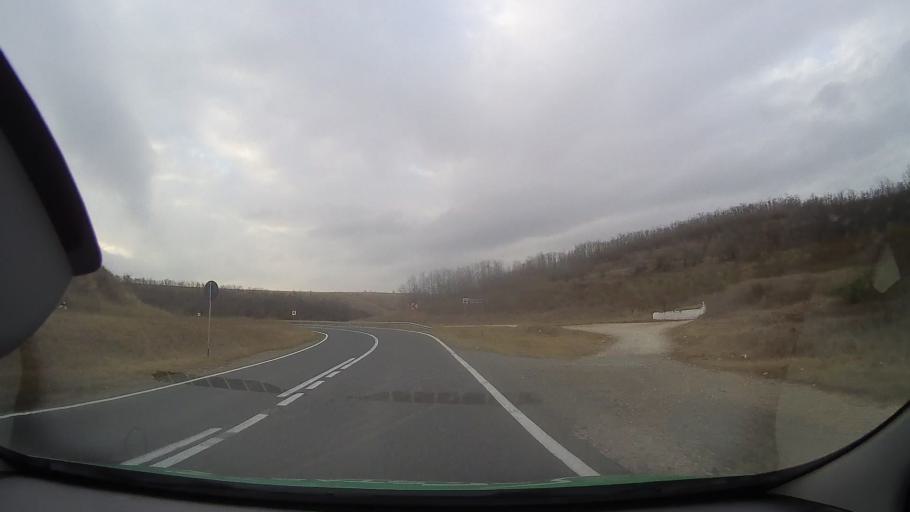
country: RO
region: Constanta
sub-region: Comuna Deleni
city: Deleni
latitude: 44.1020
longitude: 28.0268
